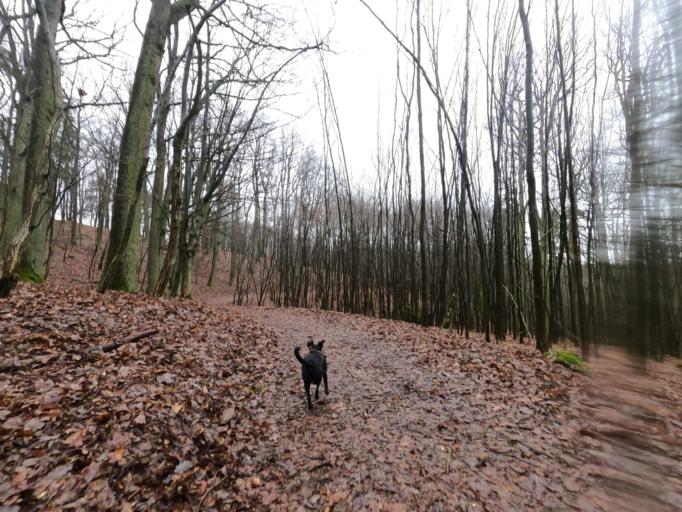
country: PL
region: Greater Poland Voivodeship
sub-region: Powiat pilski
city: Wyrzysk
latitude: 53.1270
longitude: 17.2562
